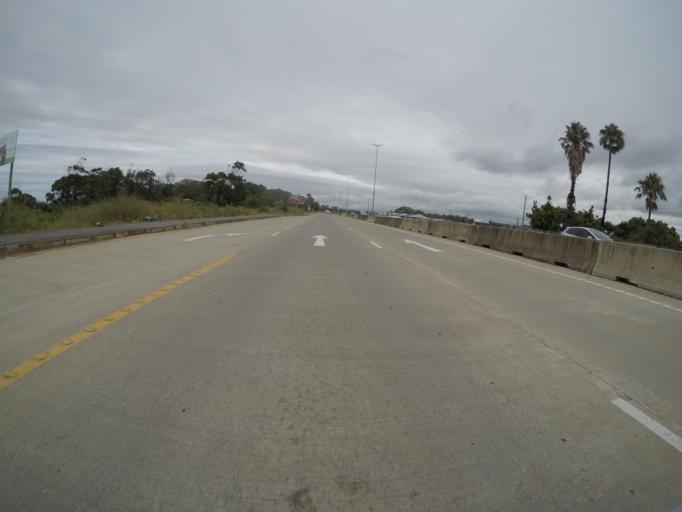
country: ZA
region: Eastern Cape
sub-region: Buffalo City Metropolitan Municipality
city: East London
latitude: -32.9413
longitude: 27.9731
